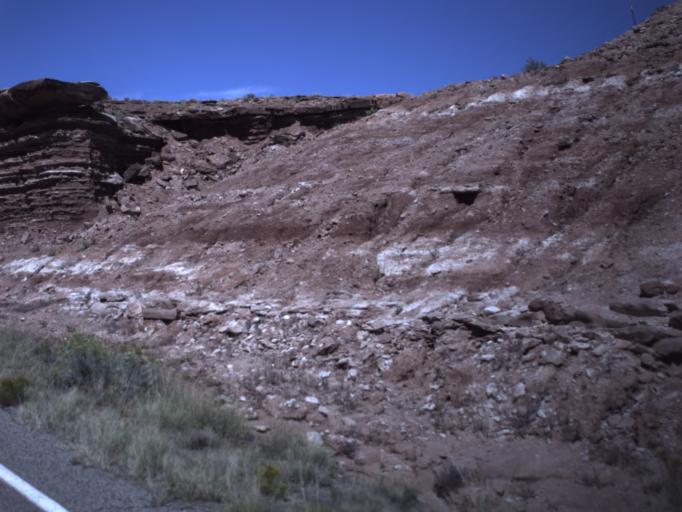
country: US
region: Utah
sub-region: San Juan County
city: Blanding
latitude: 37.2907
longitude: -109.4078
